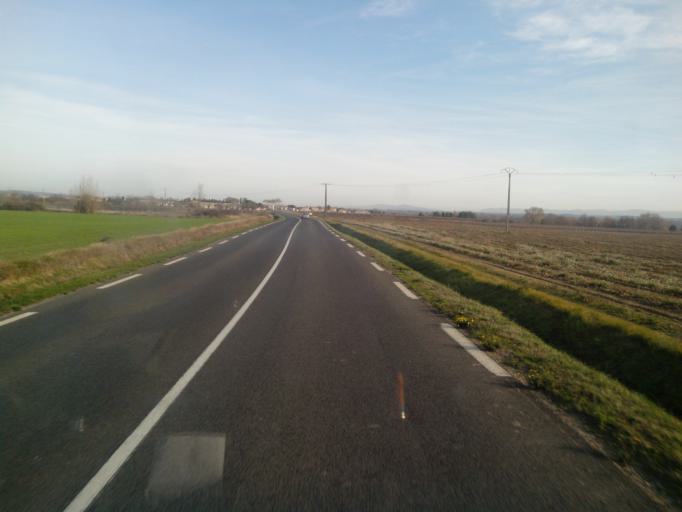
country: FR
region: Languedoc-Roussillon
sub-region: Departement de l'Aude
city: Alzonne
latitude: 43.2556
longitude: 2.1588
